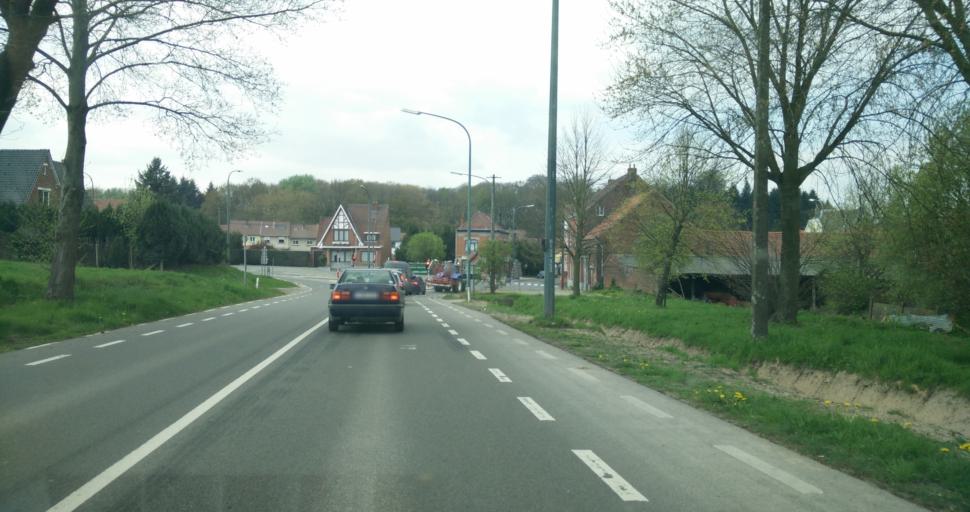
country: BE
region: Wallonia
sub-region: Province du Hainaut
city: Braine-le-Comte
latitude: 50.6552
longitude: 4.1656
